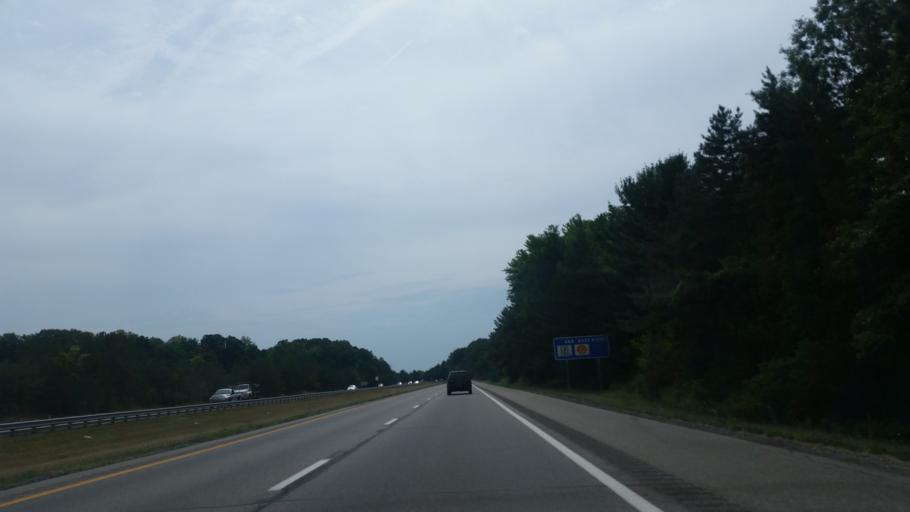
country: US
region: Ohio
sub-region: Cuyahoga County
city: Solon
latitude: 41.3980
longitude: -81.4534
